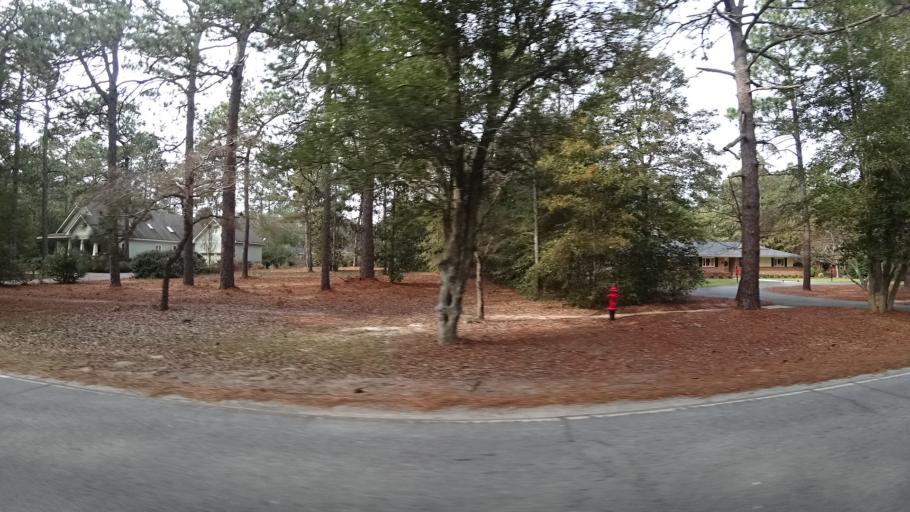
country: US
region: North Carolina
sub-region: Moore County
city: Pinehurst
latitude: 35.1983
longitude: -79.4607
